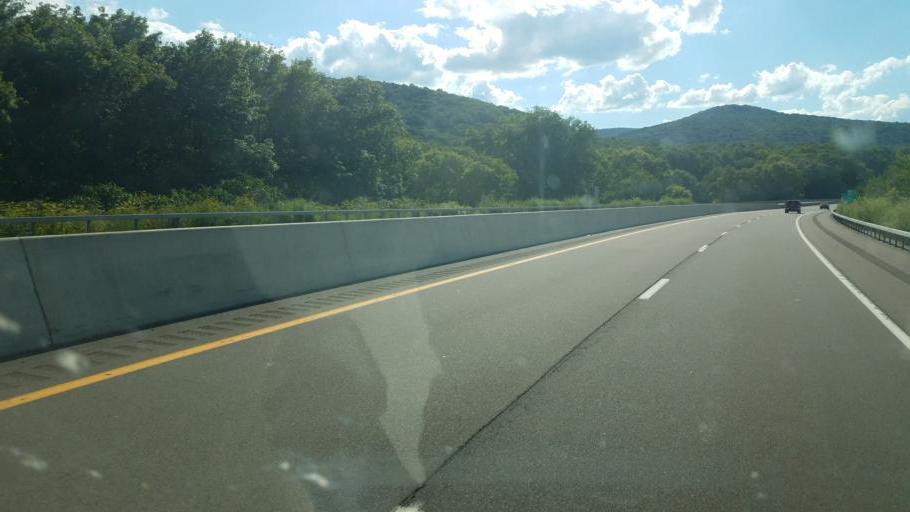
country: US
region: New York
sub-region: Cattaraugus County
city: Salamanca
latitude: 42.0916
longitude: -78.6476
